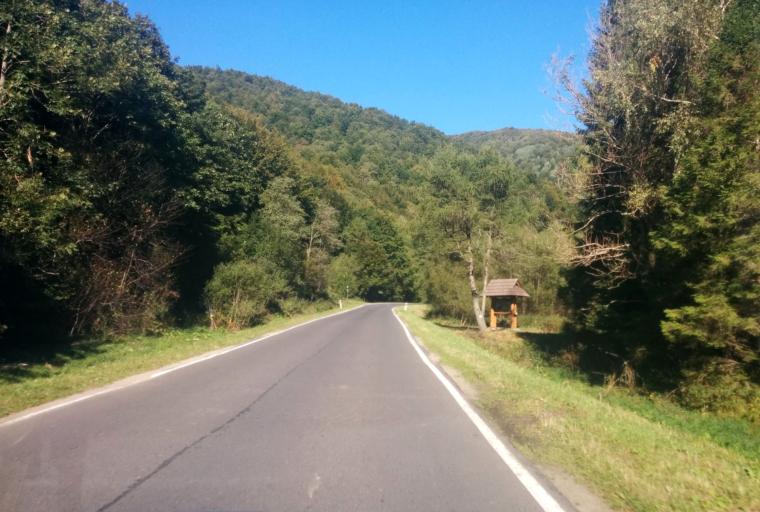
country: PL
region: Subcarpathian Voivodeship
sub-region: Powiat bieszczadzki
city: Lutowiska
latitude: 49.1418
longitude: 22.6690
